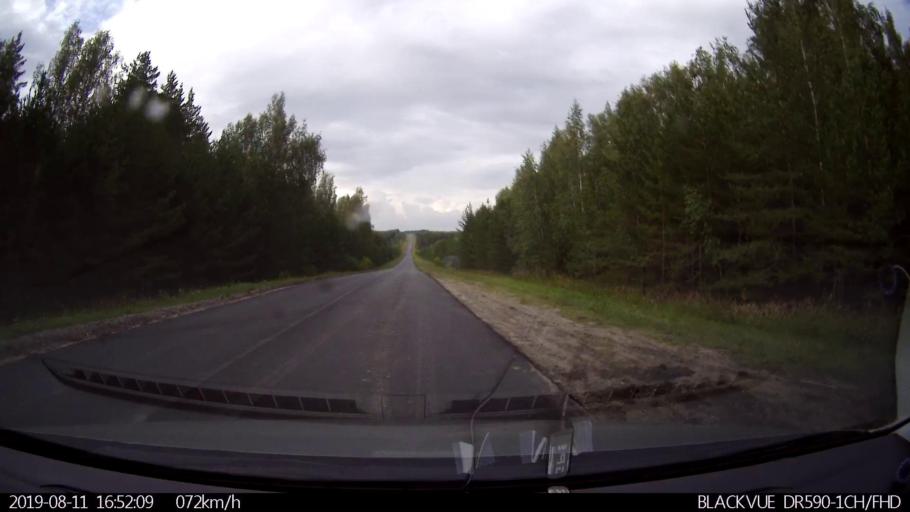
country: RU
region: Ulyanovsk
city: Mayna
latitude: 54.2448
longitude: 47.6750
